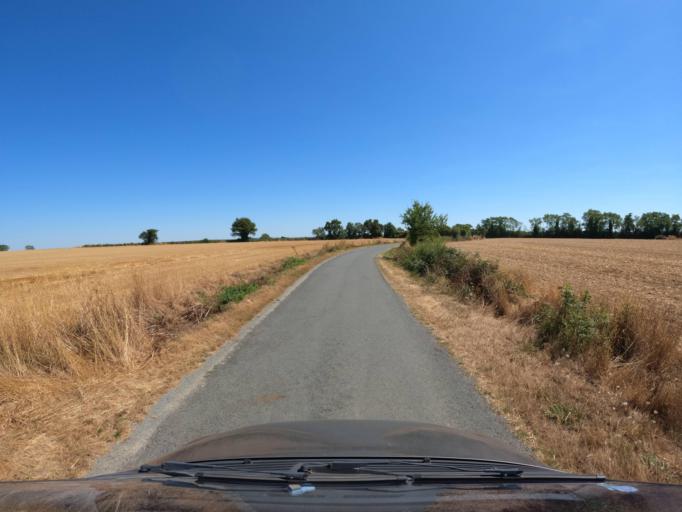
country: FR
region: Pays de la Loire
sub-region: Departement de Maine-et-Loire
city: La Seguiniere
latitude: 47.0539
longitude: -0.9686
